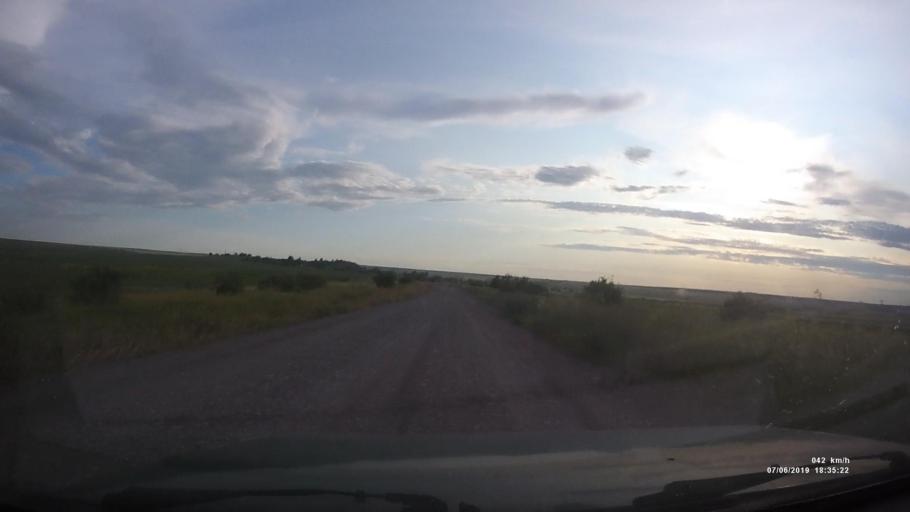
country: RU
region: Rostov
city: Staraya Stanitsa
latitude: 48.2551
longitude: 40.3604
